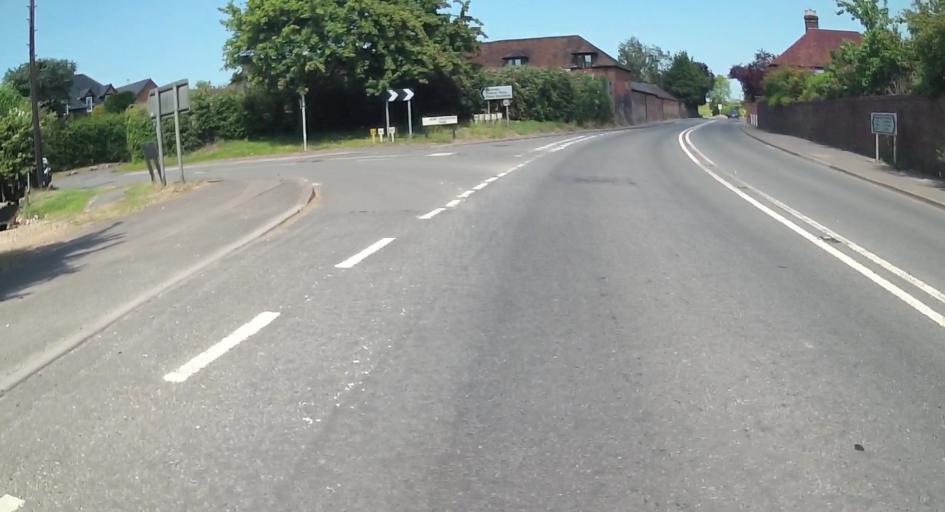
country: GB
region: England
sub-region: Hampshire
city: Basingstoke
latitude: 51.2982
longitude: -1.1146
